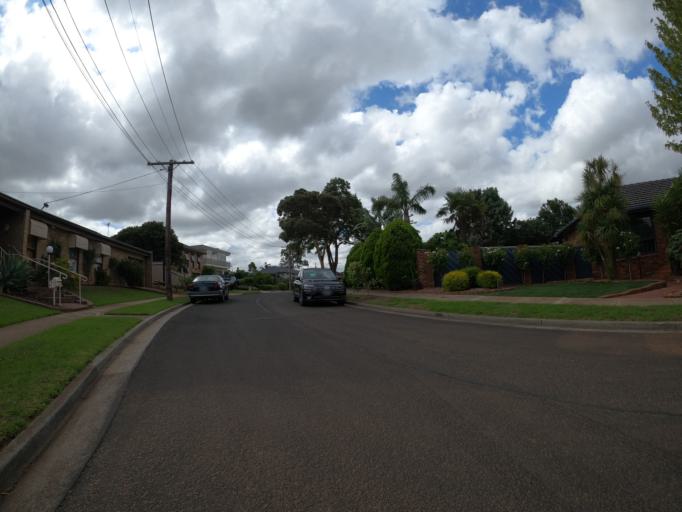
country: AU
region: Victoria
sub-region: Hume
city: Jacana
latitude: -37.6788
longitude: 144.9014
